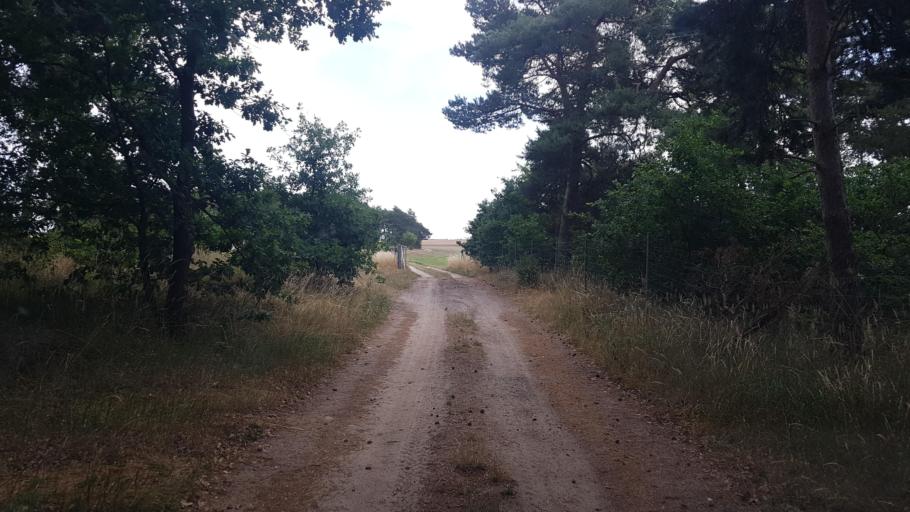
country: DE
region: Brandenburg
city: Juterbog
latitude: 51.9658
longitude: 13.0562
